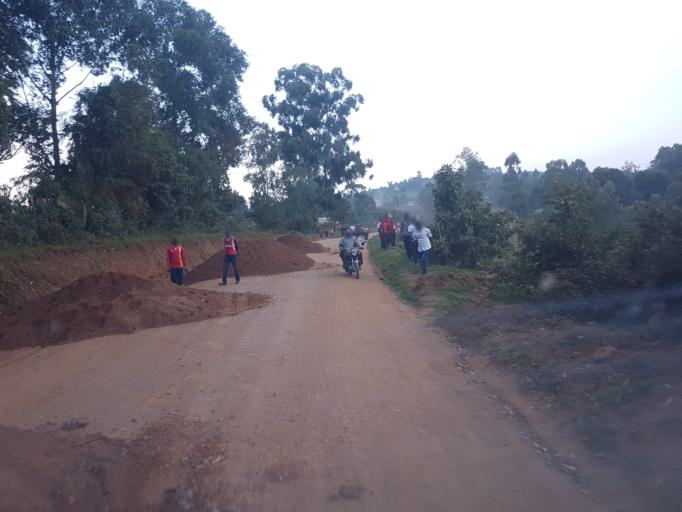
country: UG
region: Western Region
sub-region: Mitoma District
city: Mitoma
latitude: -0.6820
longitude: 29.9467
